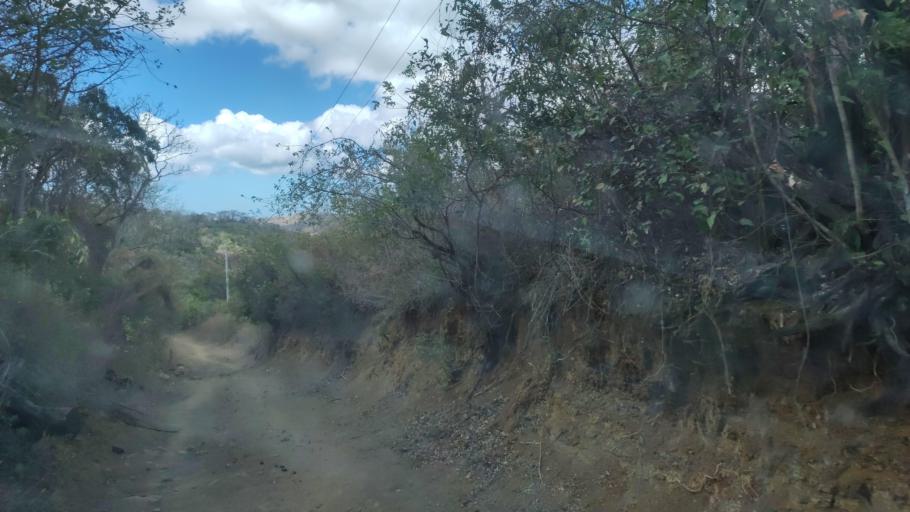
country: NI
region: Carazo
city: Santa Teresa
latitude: 11.6517
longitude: -86.2079
